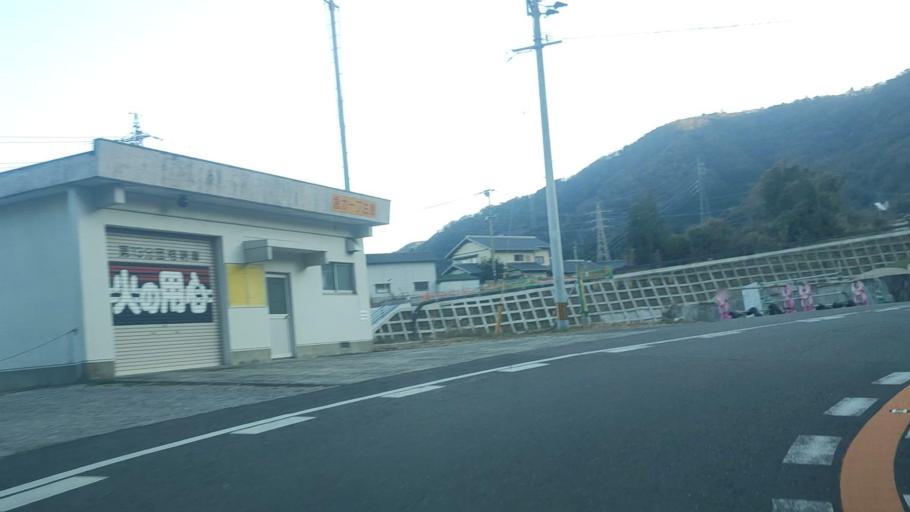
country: JP
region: Oita
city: Beppu
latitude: 33.2879
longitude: 131.4683
